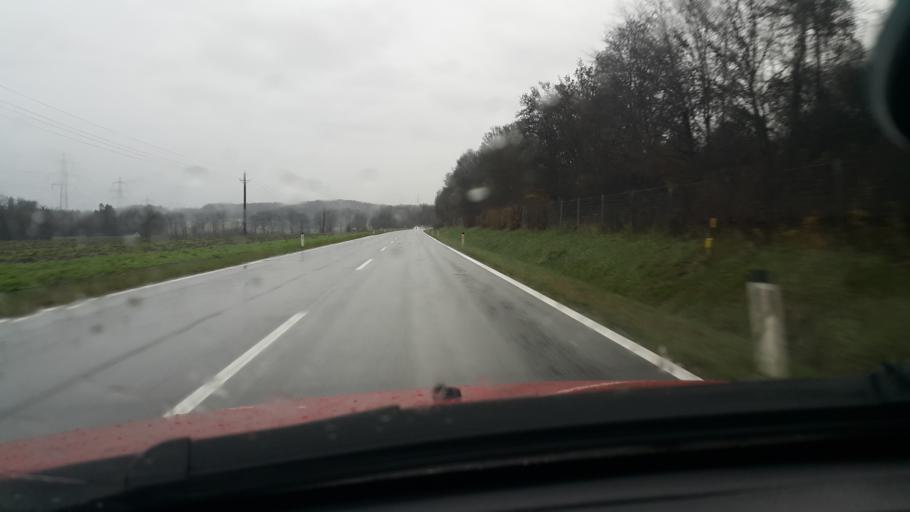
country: AT
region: Styria
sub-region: Politischer Bezirk Leibnitz
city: Lang
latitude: 46.8594
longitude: 15.5027
